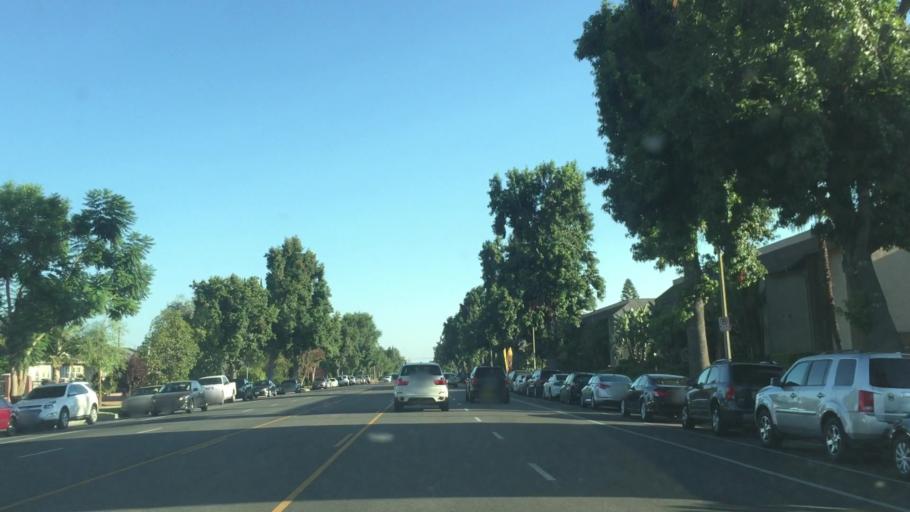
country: US
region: California
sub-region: Los Angeles County
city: San Fernando
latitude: 34.2561
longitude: -118.4850
